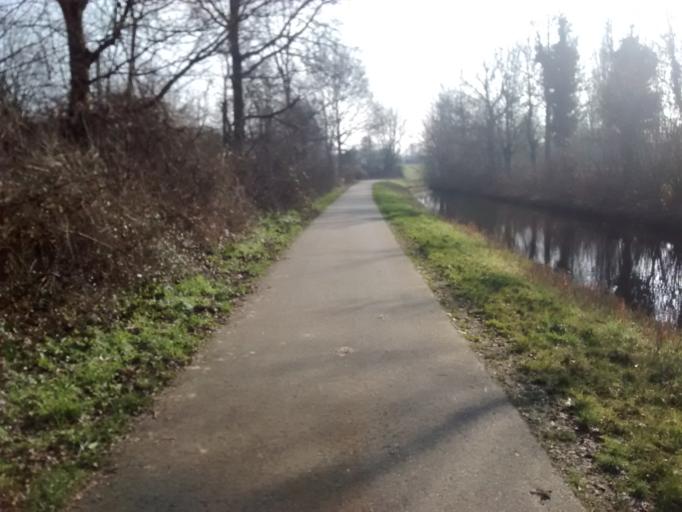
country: NL
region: Utrecht
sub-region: Gemeente Nieuwegein
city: Nieuwegein
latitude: 52.0134
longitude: 5.0886
